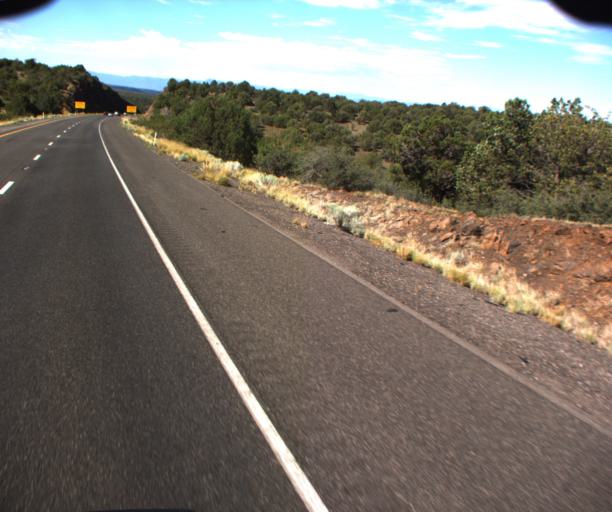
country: US
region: Arizona
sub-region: Yavapai County
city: Village of Oak Creek (Big Park)
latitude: 34.7934
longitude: -111.6012
